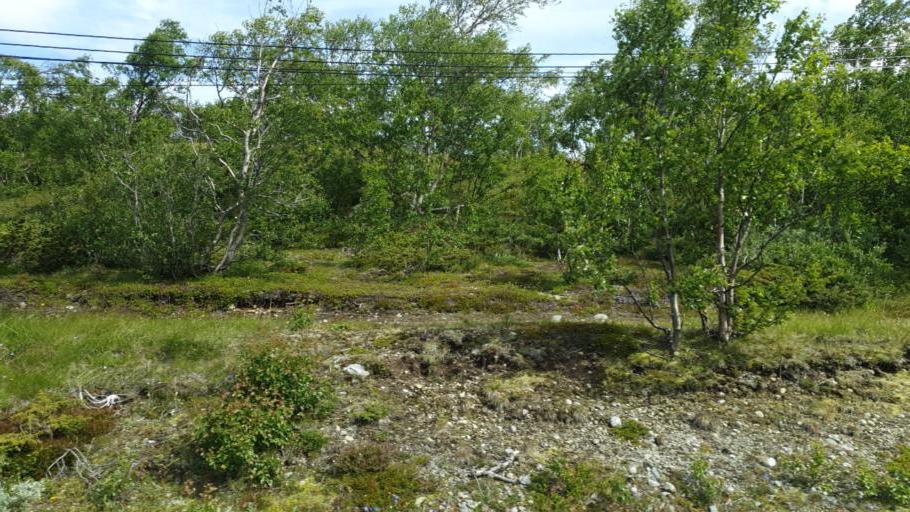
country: NO
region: Oppland
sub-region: Oystre Slidre
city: Heggenes
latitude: 61.4884
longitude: 8.8276
